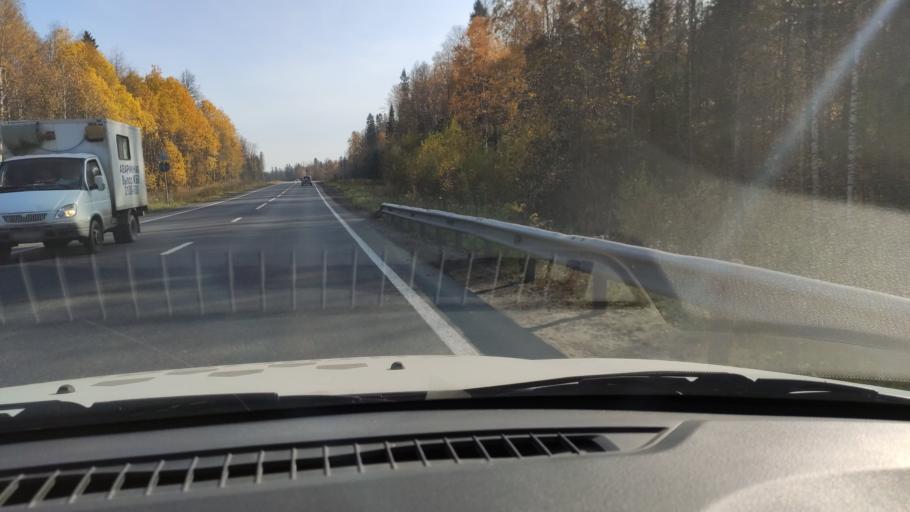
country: RU
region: Perm
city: Novyye Lyady
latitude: 58.0285
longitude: 56.4987
